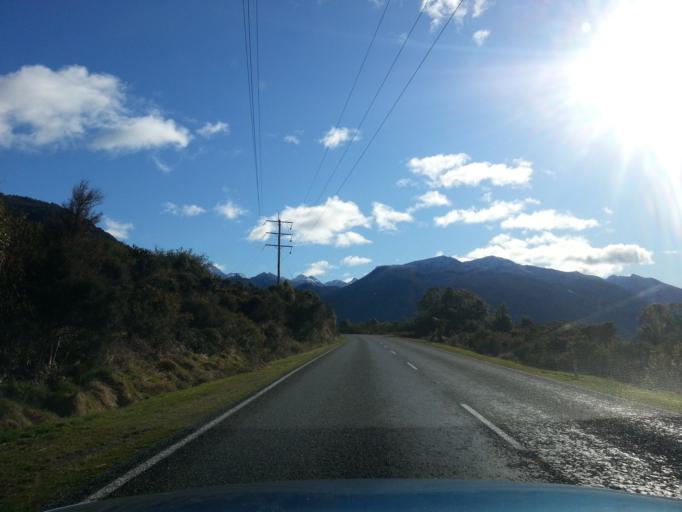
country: NZ
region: West Coast
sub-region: Grey District
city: Greymouth
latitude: -42.7428
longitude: 171.4725
